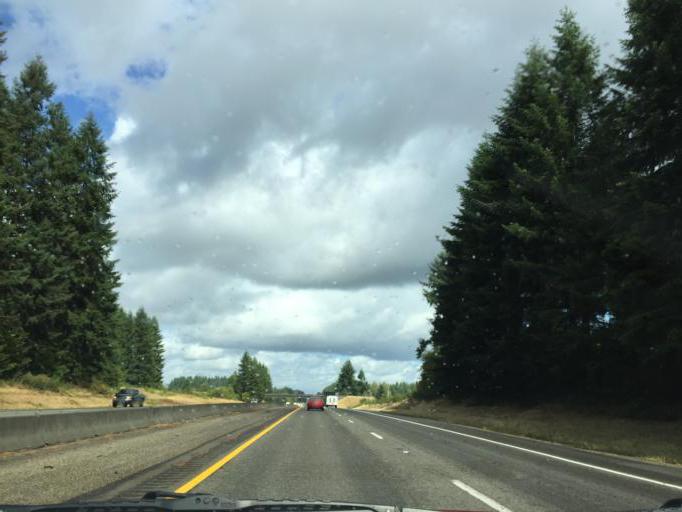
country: US
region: Washington
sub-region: Lewis County
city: Winlock
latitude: 46.5143
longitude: -122.8766
